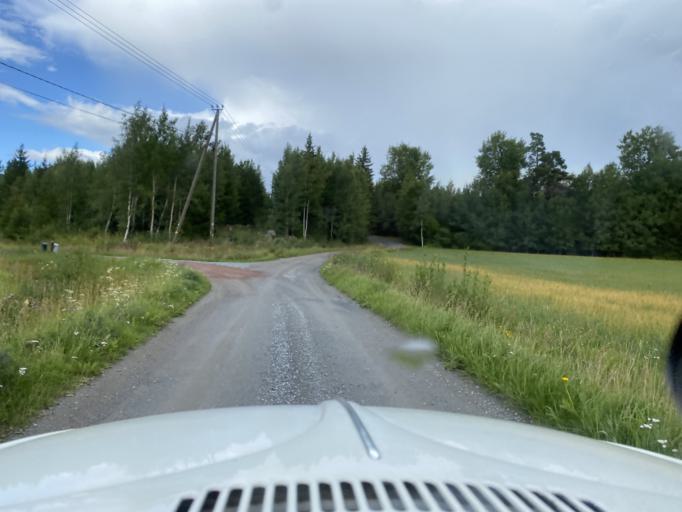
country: FI
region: Pirkanmaa
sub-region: Lounais-Pirkanmaa
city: Punkalaidun
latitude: 61.1263
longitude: 23.0637
